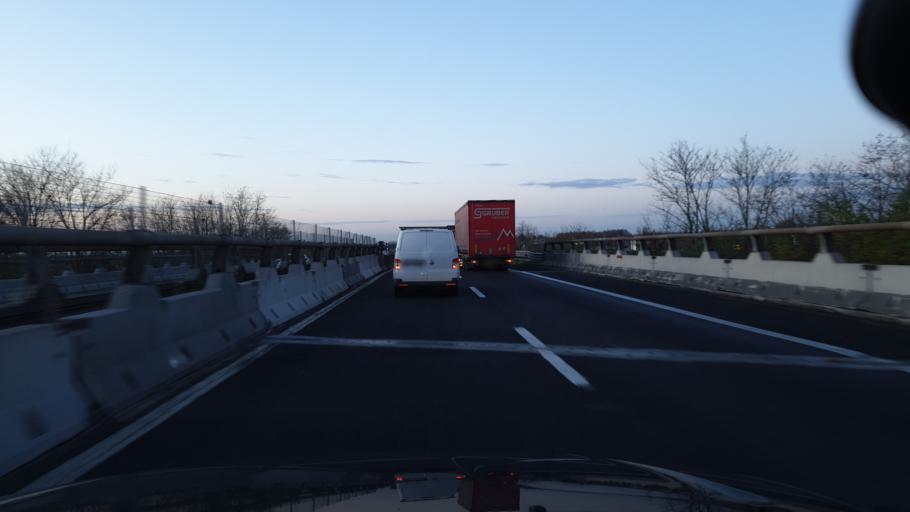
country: IT
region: Veneto
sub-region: Provincia di Rovigo
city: Villamarzana
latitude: 45.0049
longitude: 11.6788
